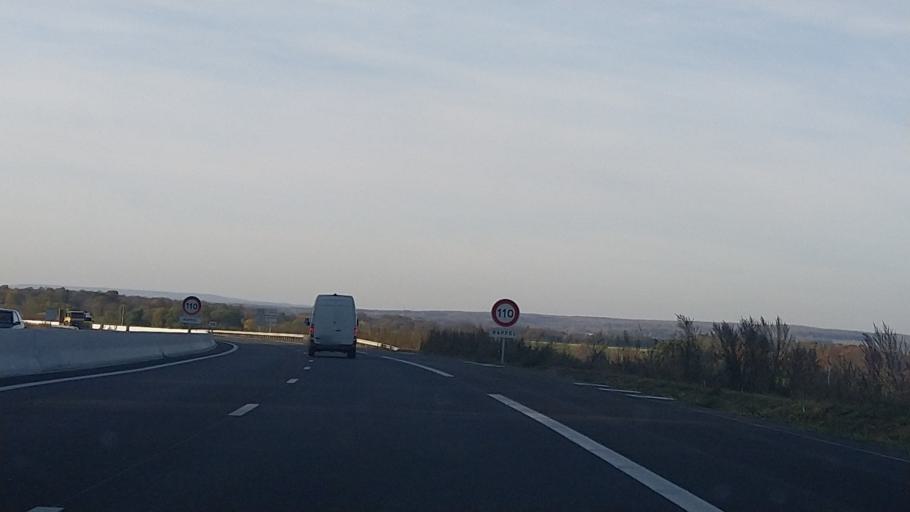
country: FR
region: Ile-de-France
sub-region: Departement du Val-d'Oise
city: Maffliers
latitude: 49.0968
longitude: 2.2957
